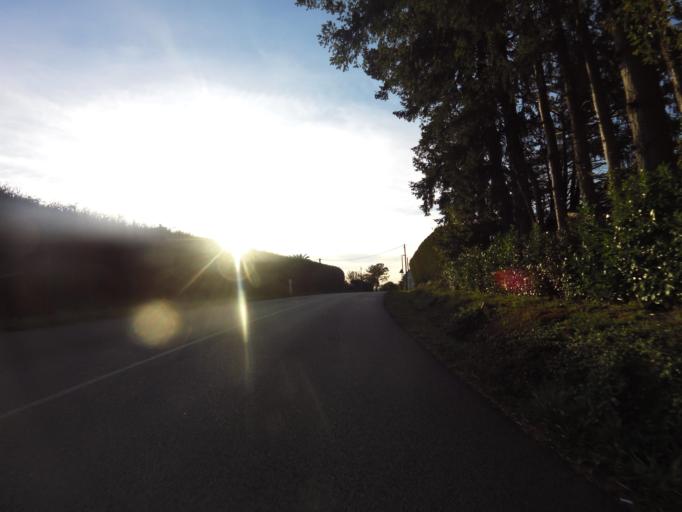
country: FR
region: Brittany
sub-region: Departement du Morbihan
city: Trefflean
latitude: 47.6370
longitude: -2.6042
